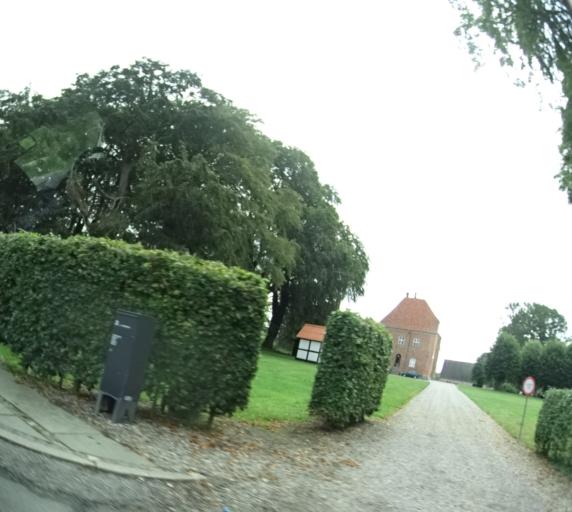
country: DK
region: Central Jutland
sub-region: Syddjurs Kommune
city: Ryomgard
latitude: 56.3786
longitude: 10.5015
